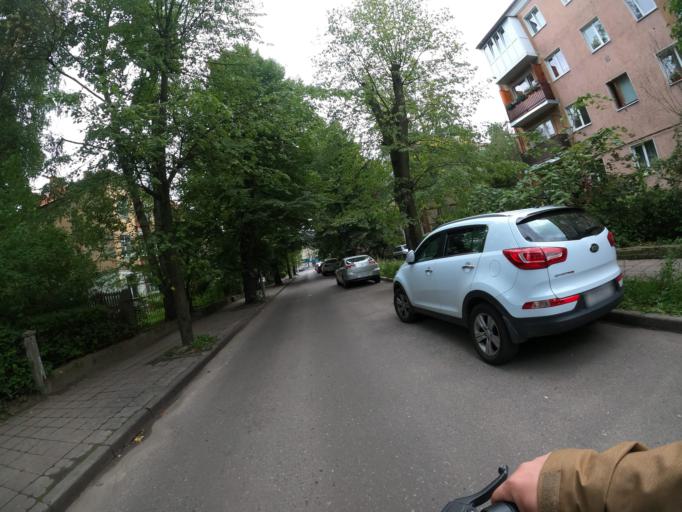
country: RU
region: Kaliningrad
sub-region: Gorod Kaliningrad
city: Kaliningrad
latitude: 54.7222
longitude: 20.4730
